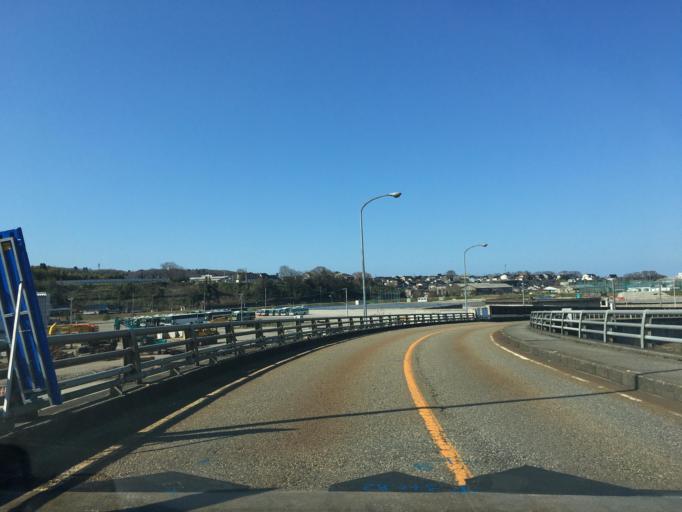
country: JP
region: Toyama
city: Nishishinminato
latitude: 36.7811
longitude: 137.0485
